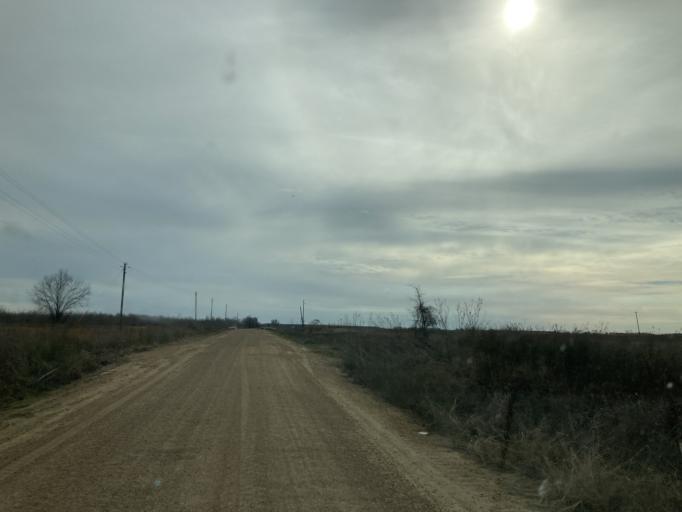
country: US
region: Mississippi
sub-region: Humphreys County
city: Belzoni
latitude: 33.1694
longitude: -90.5723
